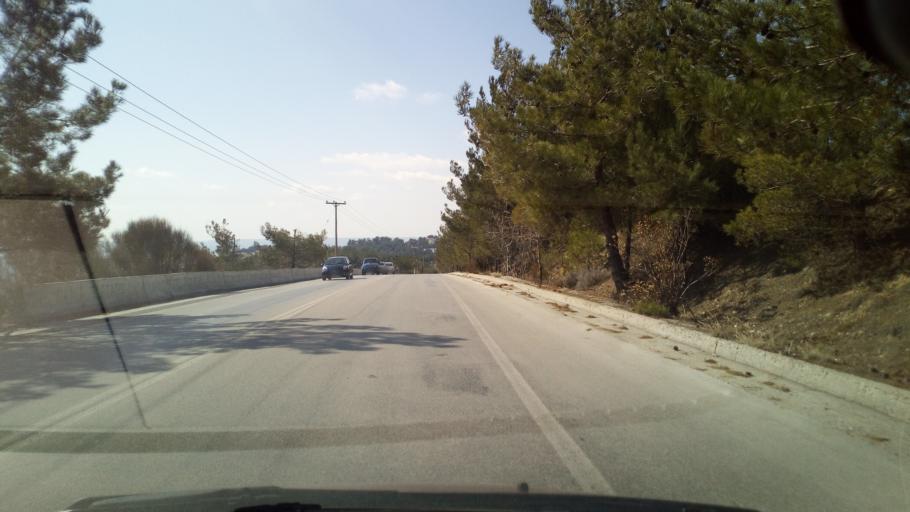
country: GR
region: Central Macedonia
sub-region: Nomos Thessalonikis
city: Panorama
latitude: 40.6050
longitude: 23.0507
